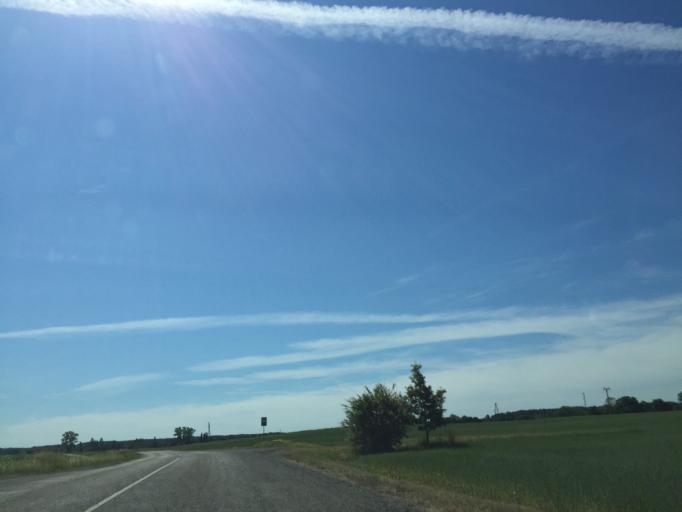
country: LV
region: Aizpute
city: Aizpute
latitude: 56.7048
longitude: 21.7731
